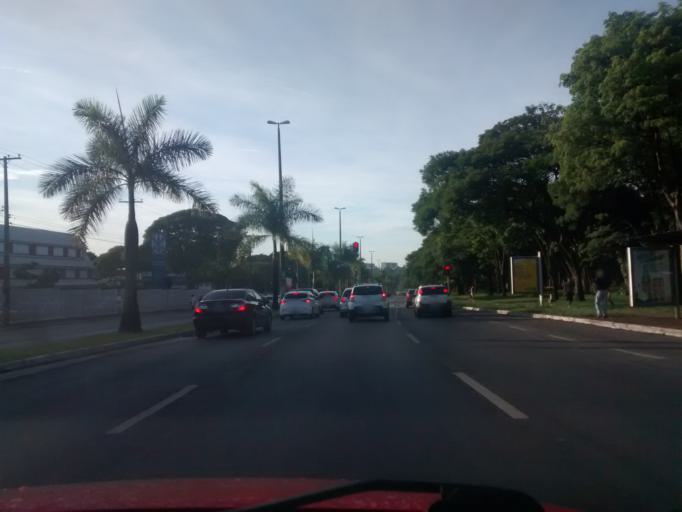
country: BR
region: Federal District
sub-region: Brasilia
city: Brasilia
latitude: -15.7744
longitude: -47.8746
